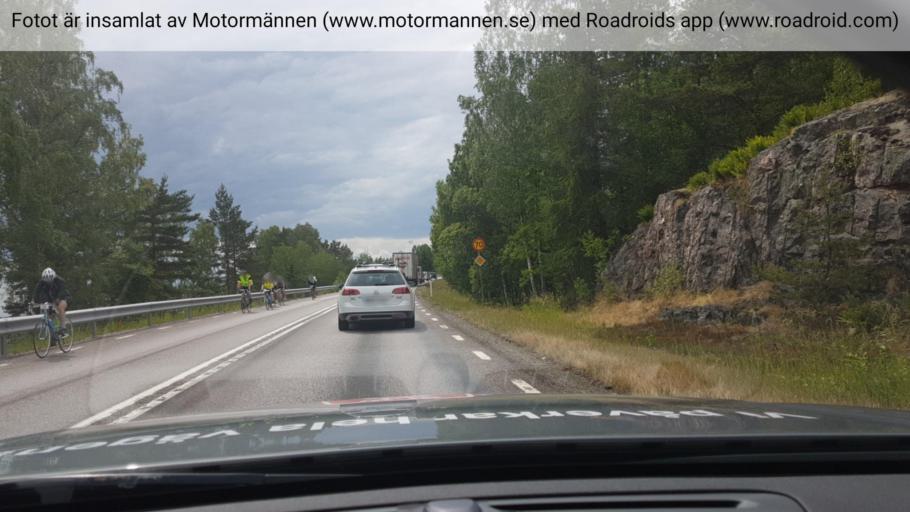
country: SE
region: OErebro
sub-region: Askersunds Kommun
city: Askersund
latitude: 58.7204
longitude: 14.7562
